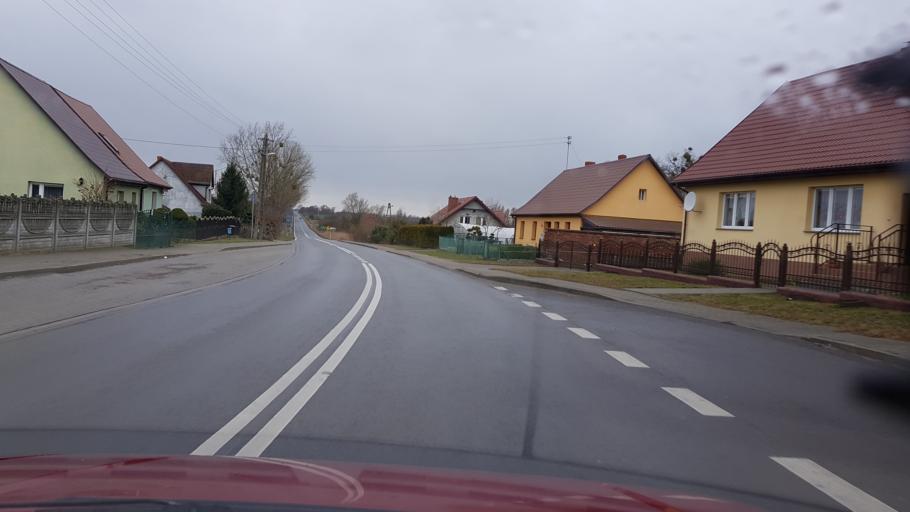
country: PL
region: West Pomeranian Voivodeship
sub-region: Powiat pyrzycki
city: Bielice
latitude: 53.2611
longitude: 14.6182
